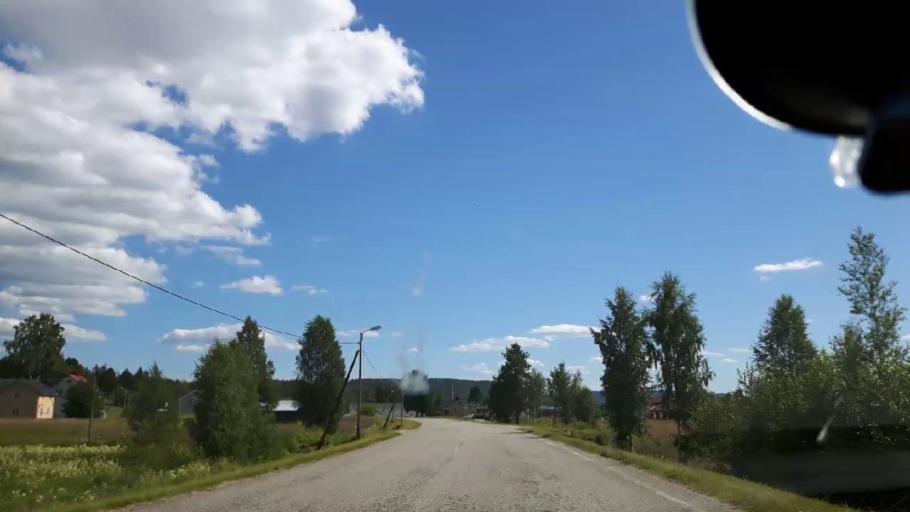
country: SE
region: Vaesternorrland
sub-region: Ange Kommun
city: Fransta
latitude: 62.7947
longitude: 16.2108
